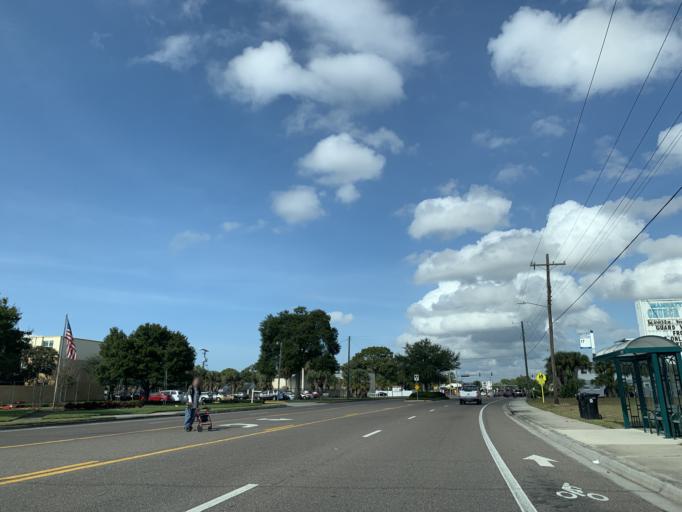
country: US
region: Florida
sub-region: Hillsborough County
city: Tampa
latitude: 27.9052
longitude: -82.5184
